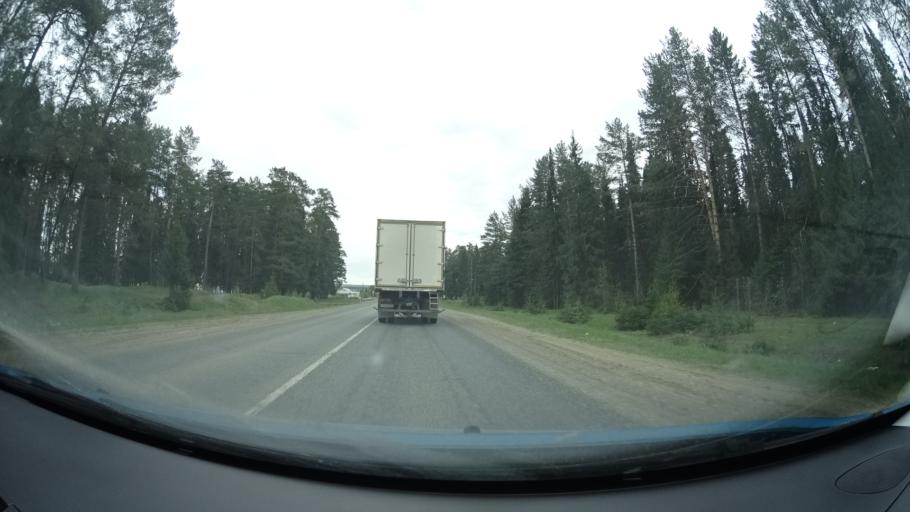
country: RU
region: Perm
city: Yugo-Kamskiy
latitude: 57.5604
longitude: 55.6803
